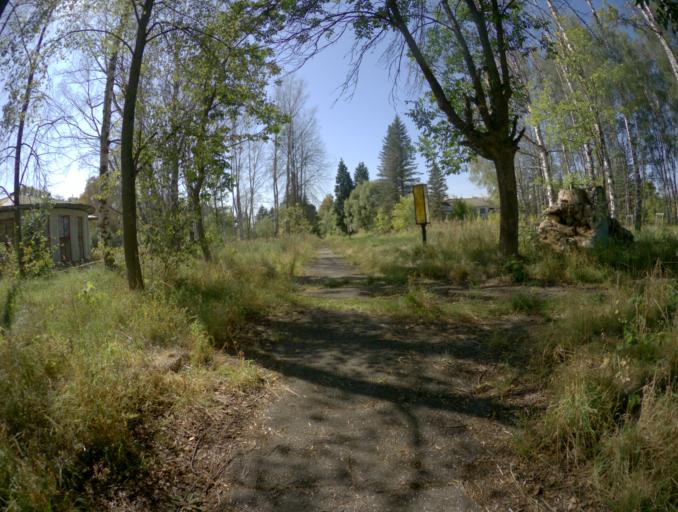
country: RU
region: Vladimir
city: Sobinka
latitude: 55.9436
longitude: 39.9862
